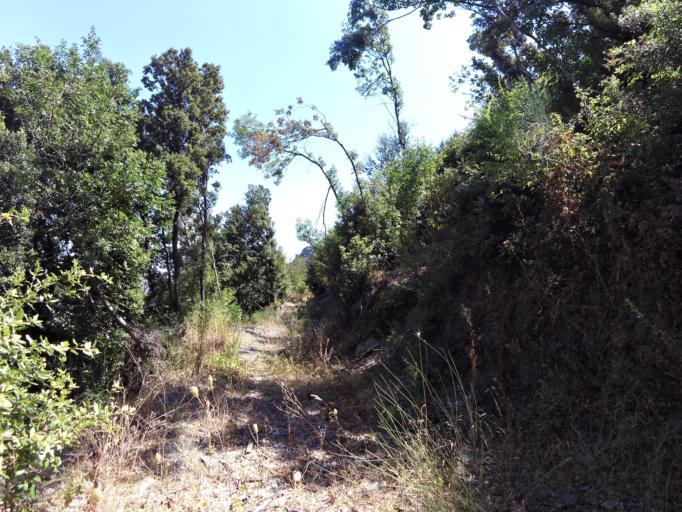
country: IT
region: Calabria
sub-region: Provincia di Reggio Calabria
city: Pazzano
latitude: 38.4699
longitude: 16.4355
